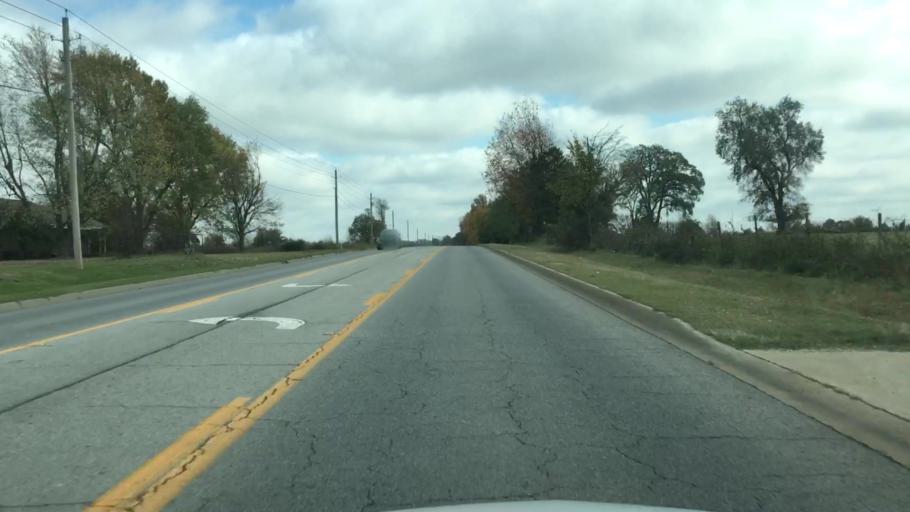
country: US
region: Arkansas
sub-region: Benton County
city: Siloam Springs
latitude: 36.1953
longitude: -94.5033
